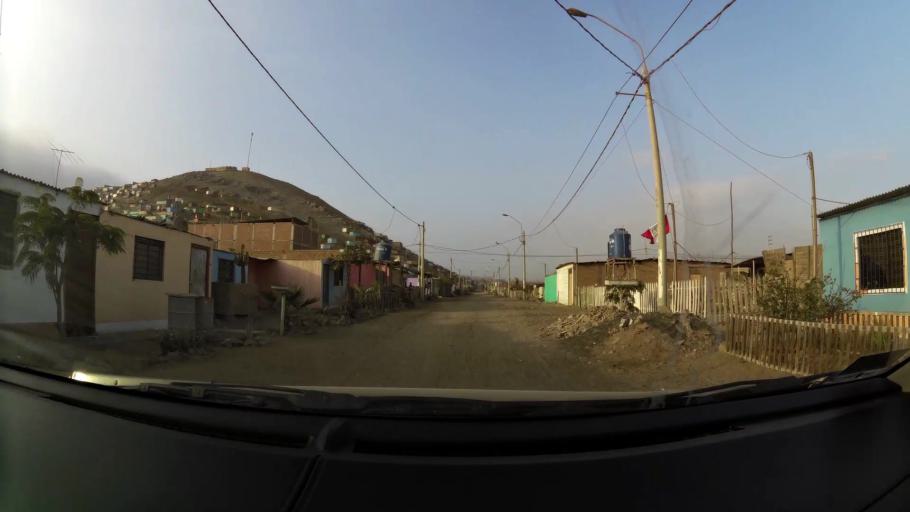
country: PE
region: Lima
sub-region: Lima
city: Santa Rosa
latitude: -11.7449
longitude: -77.1498
